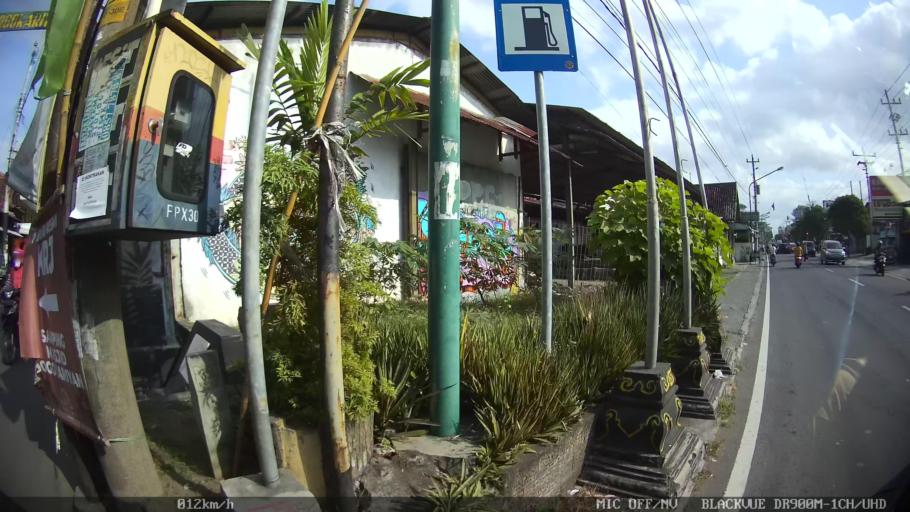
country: ID
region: Daerah Istimewa Yogyakarta
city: Kasihan
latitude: -7.8255
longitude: 110.3674
